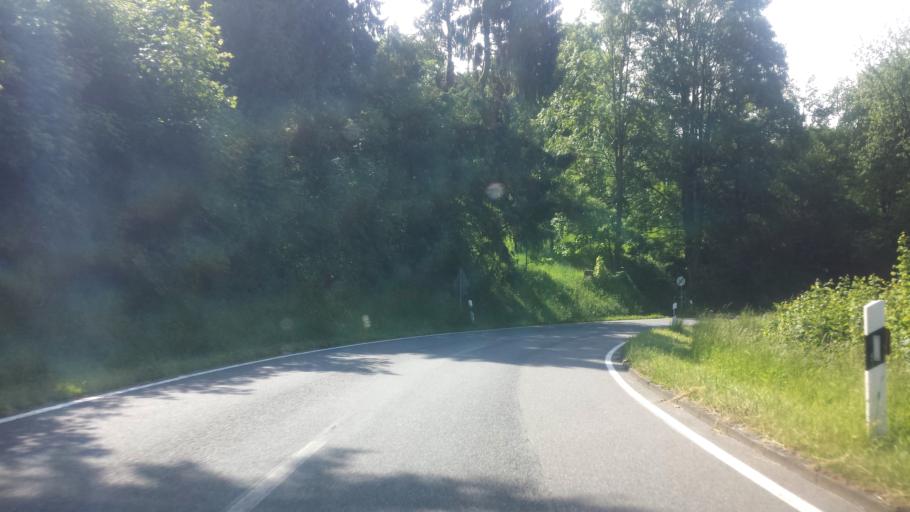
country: DE
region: Hesse
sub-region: Regierungsbezirk Darmstadt
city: Wald-Michelbach
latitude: 49.5777
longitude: 8.8011
